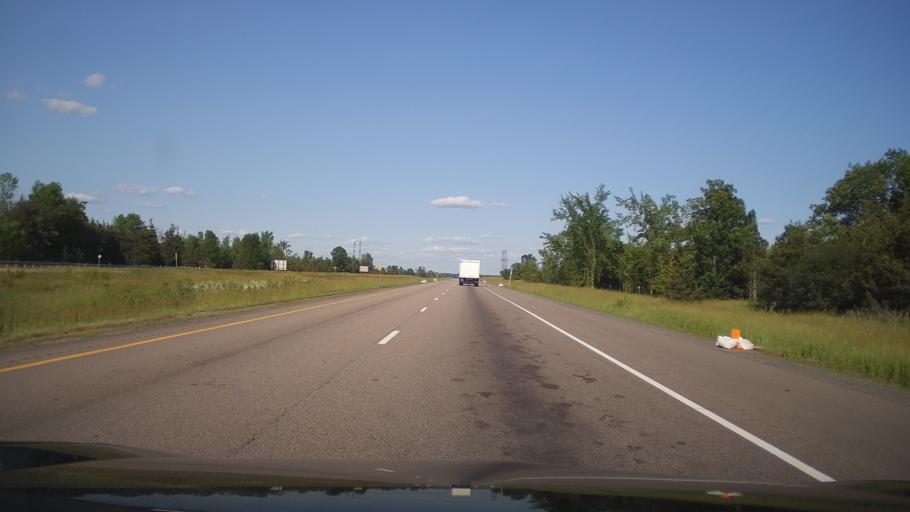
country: CA
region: Ontario
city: Deseronto
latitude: 44.2492
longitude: -77.0274
